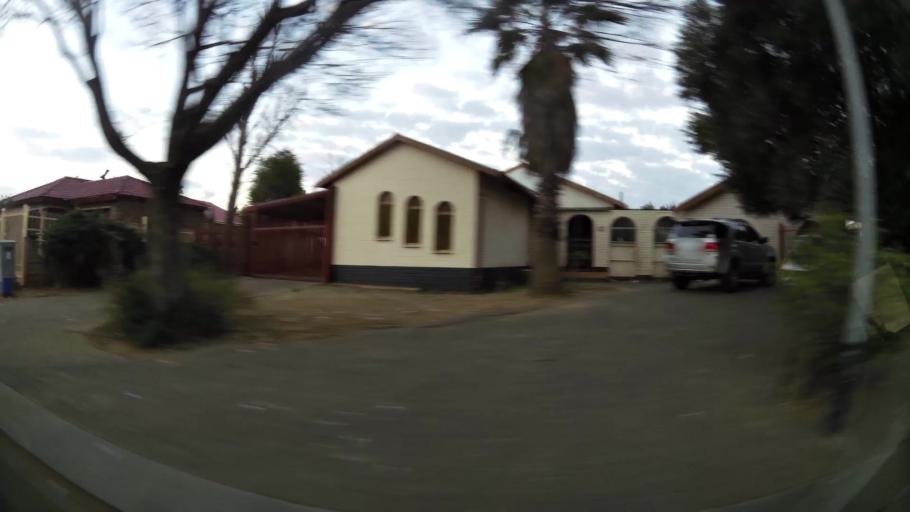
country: ZA
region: Orange Free State
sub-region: Mangaung Metropolitan Municipality
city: Bloemfontein
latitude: -29.1709
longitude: 26.1888
